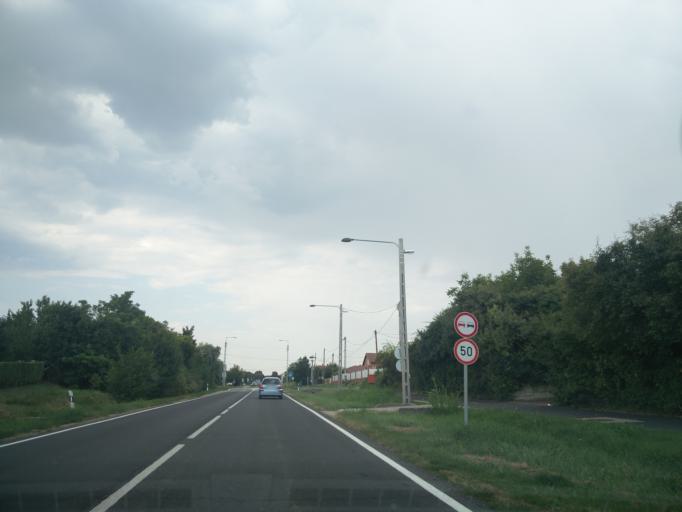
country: HU
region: Fejer
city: Polgardi
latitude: 47.0573
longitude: 18.3066
